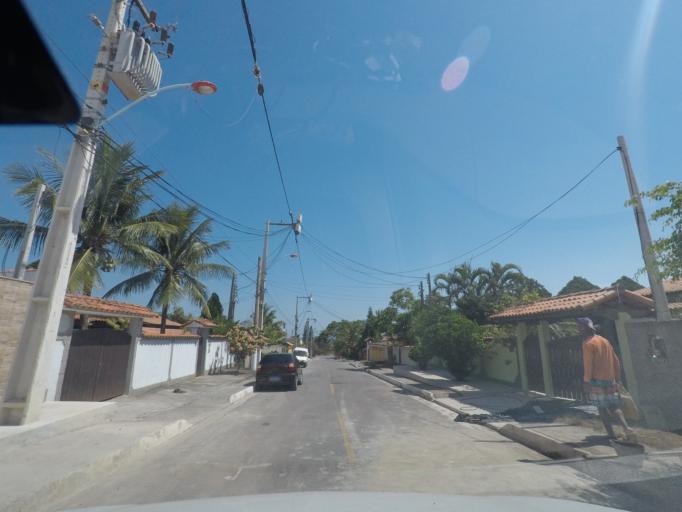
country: BR
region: Rio de Janeiro
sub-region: Marica
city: Marica
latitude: -22.9661
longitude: -42.9649
